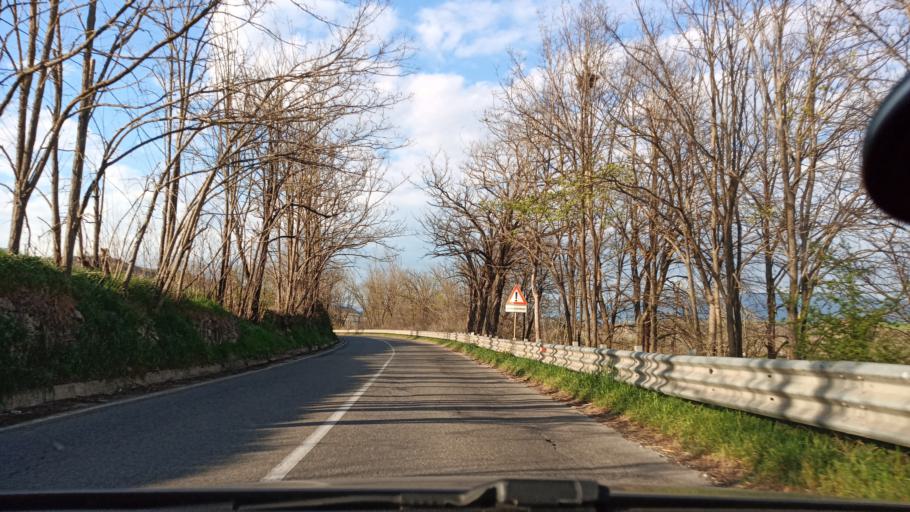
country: IT
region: Latium
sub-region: Citta metropolitana di Roma Capitale
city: Fiano Romano
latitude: 42.1839
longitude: 12.6051
